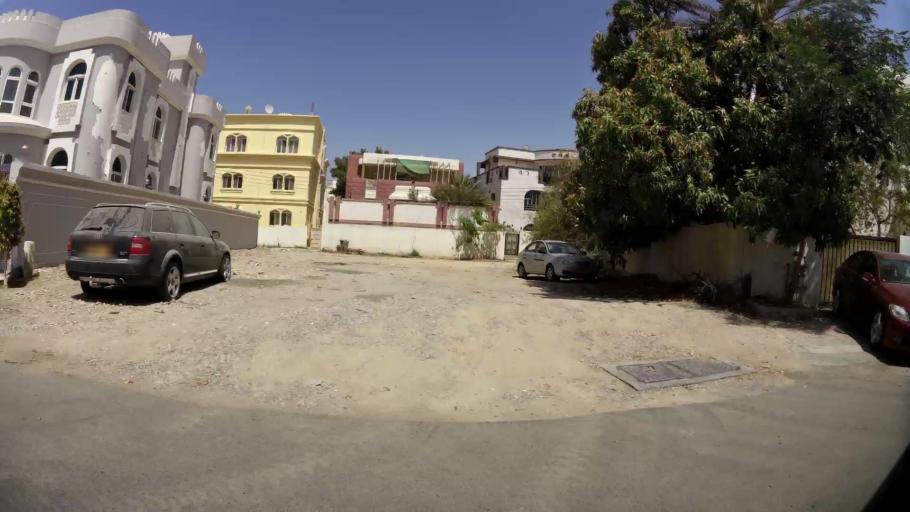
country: OM
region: Muhafazat Masqat
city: Muscat
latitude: 23.6141
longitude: 58.4989
